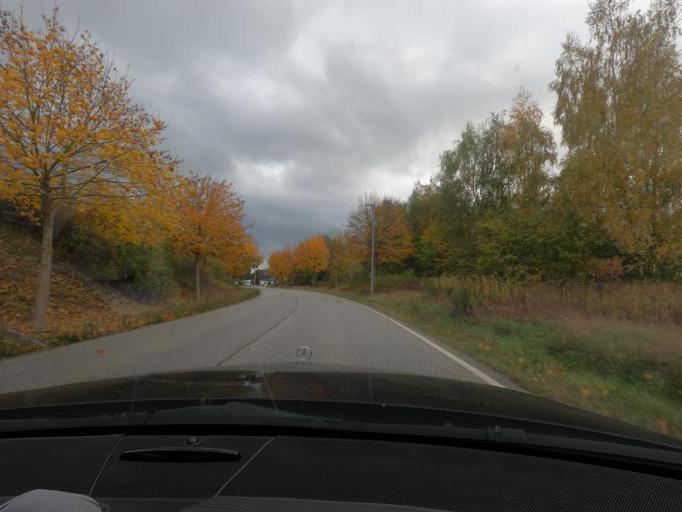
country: DE
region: Schleswig-Holstein
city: Geesthacht
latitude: 53.4512
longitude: 10.3676
